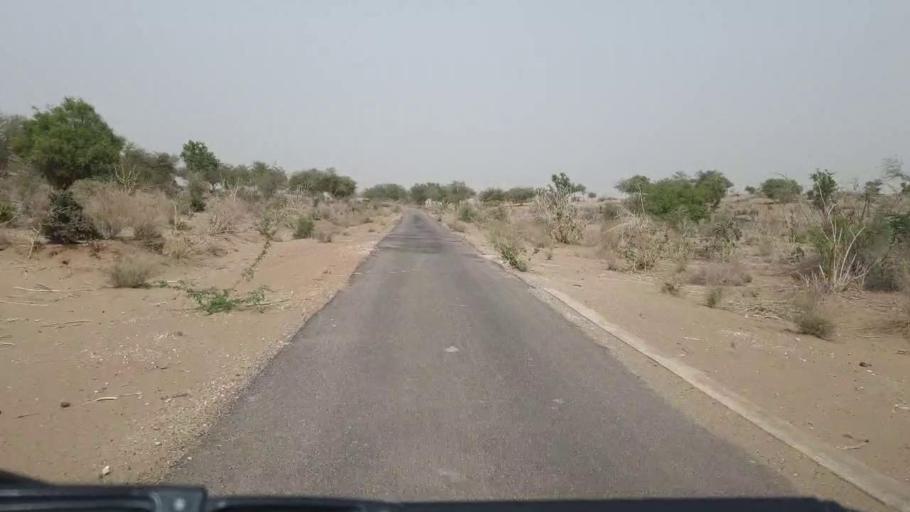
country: PK
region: Sindh
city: Islamkot
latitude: 25.3729
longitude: 70.5302
